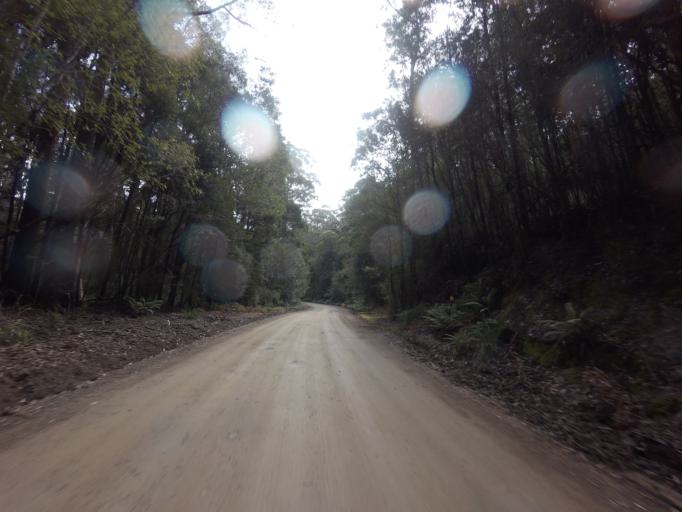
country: AU
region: Tasmania
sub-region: Huon Valley
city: Geeveston
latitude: -43.3915
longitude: 146.8536
